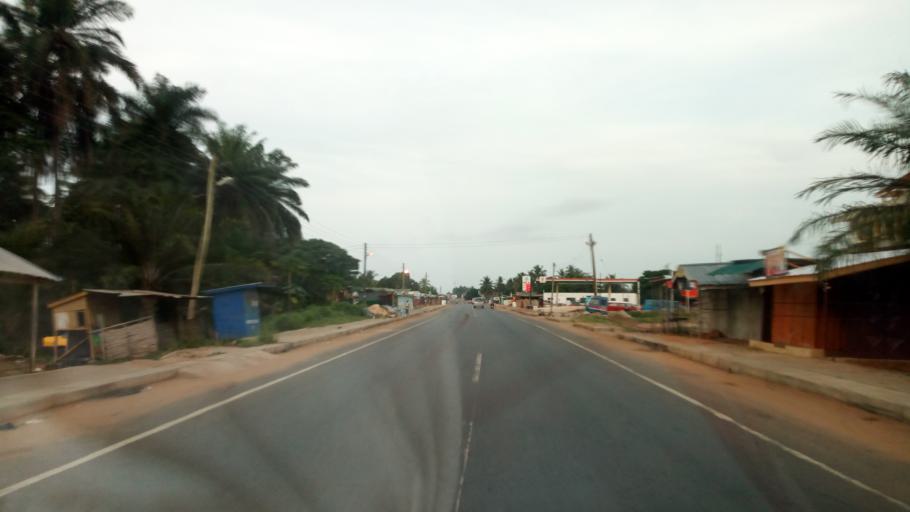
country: TG
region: Maritime
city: Lome
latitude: 6.1092
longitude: 1.1569
